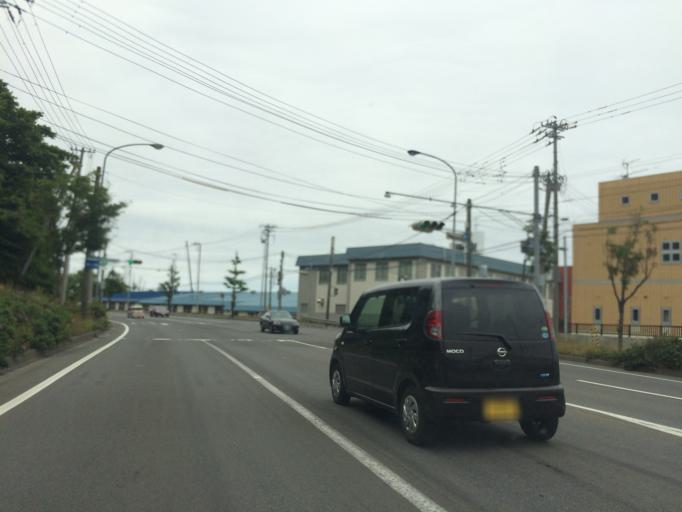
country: JP
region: Hokkaido
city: Otaru
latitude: 43.1374
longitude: 141.1692
